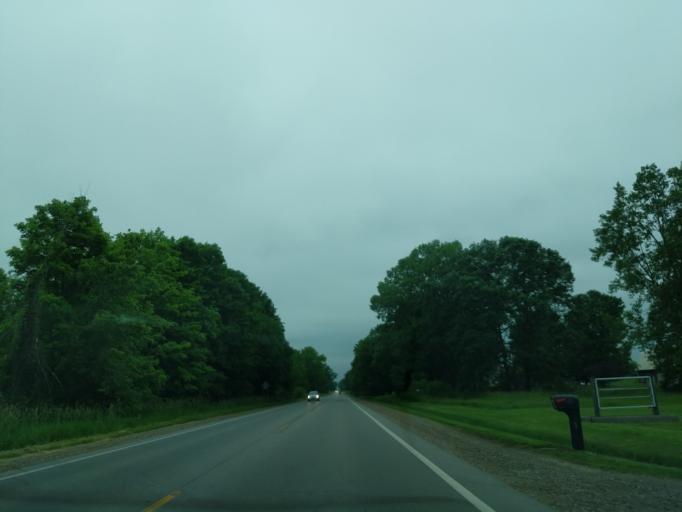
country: US
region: Michigan
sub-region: Branch County
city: Quincy
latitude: 41.9485
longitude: -84.8157
